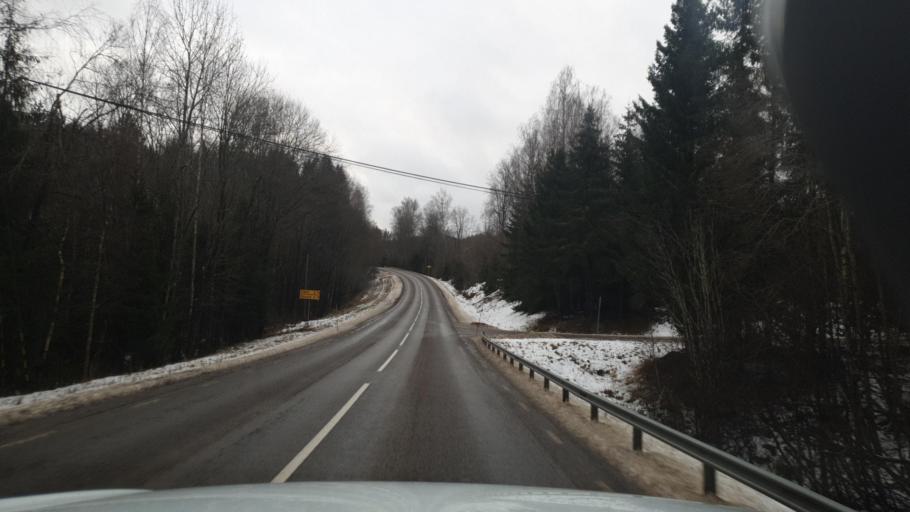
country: SE
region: Vaermland
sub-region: Eda Kommun
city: Amotfors
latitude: 59.7395
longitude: 12.3819
